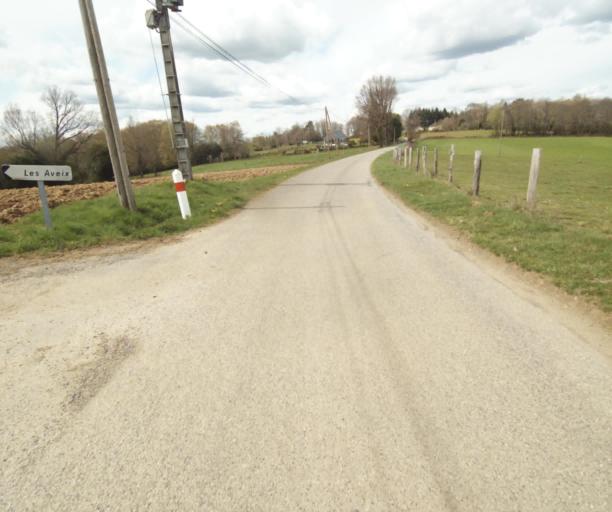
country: FR
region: Limousin
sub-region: Departement de la Correze
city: Laguenne
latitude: 45.2262
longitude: 1.8805
